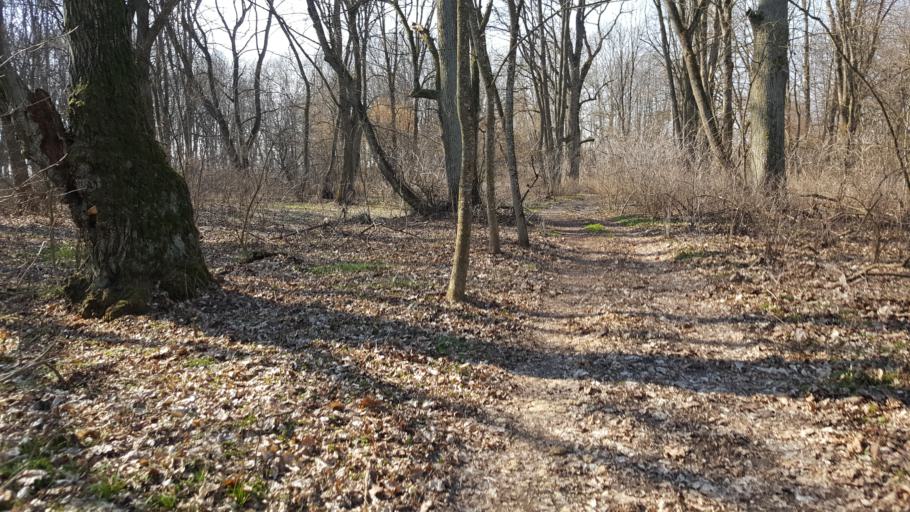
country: BY
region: Brest
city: Zhabinka
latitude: 52.3151
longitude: 23.9285
